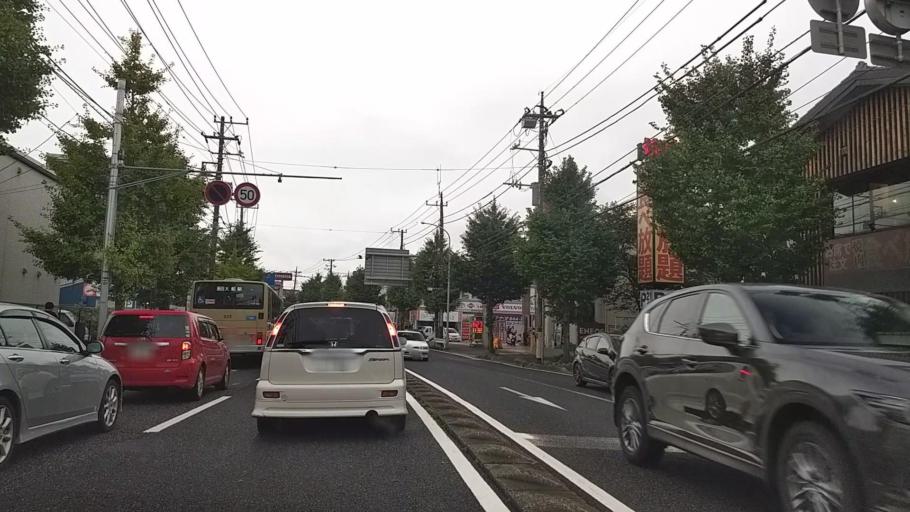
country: JP
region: Kanagawa
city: Yokohama
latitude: 35.3925
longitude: 139.5834
